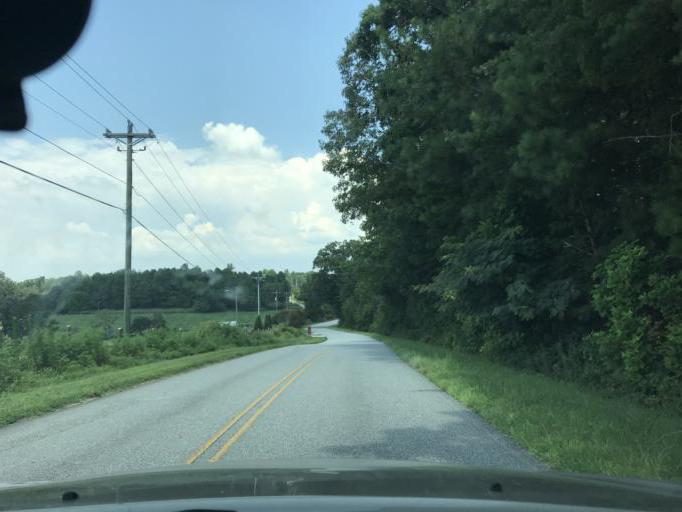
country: US
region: Georgia
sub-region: Dawson County
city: Dawsonville
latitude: 34.3418
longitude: -84.0791
